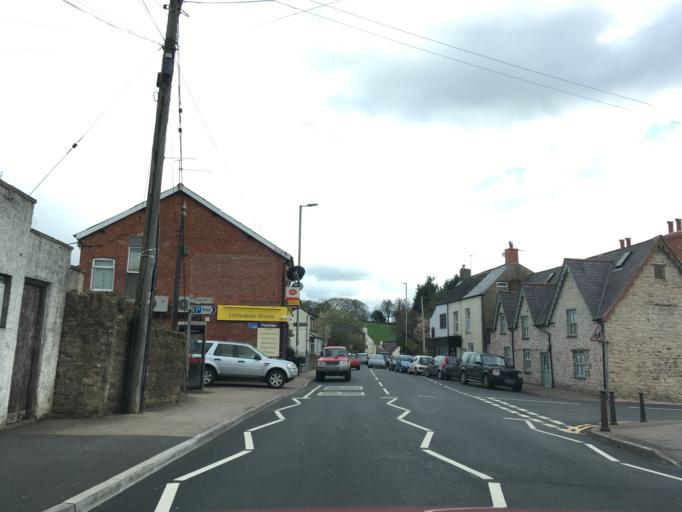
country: GB
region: England
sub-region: Gloucestershire
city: Cinderford
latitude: 51.8193
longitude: -2.4810
